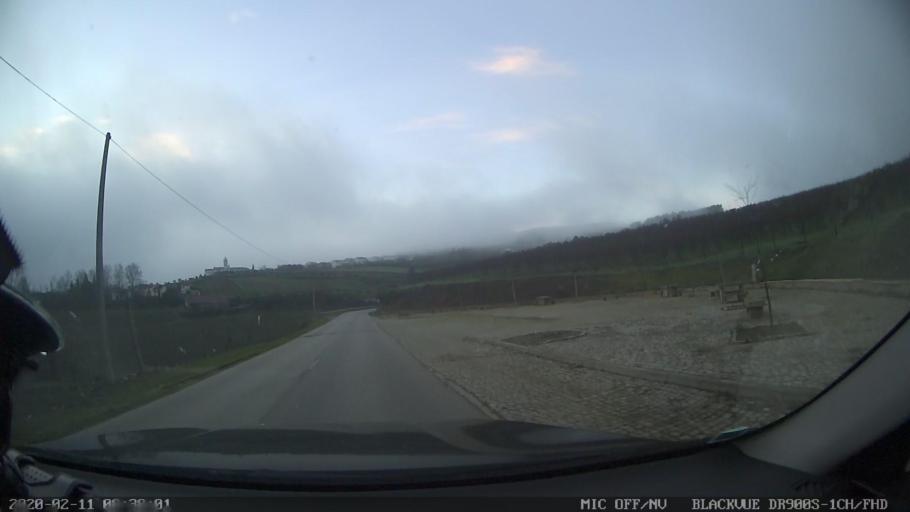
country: PT
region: Vila Real
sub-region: Sabrosa
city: Sabrosa
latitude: 41.2516
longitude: -7.5853
